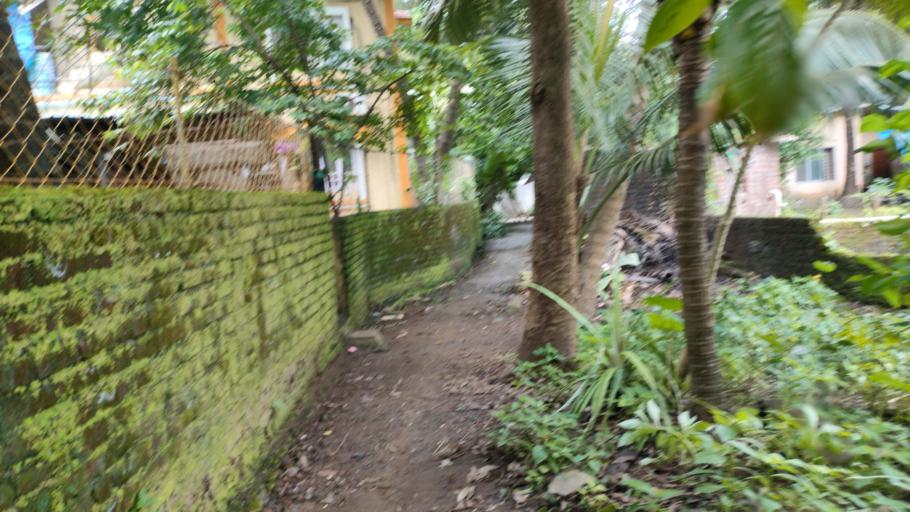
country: IN
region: Maharashtra
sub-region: Thane
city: Virar
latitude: 19.3694
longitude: 72.7944
